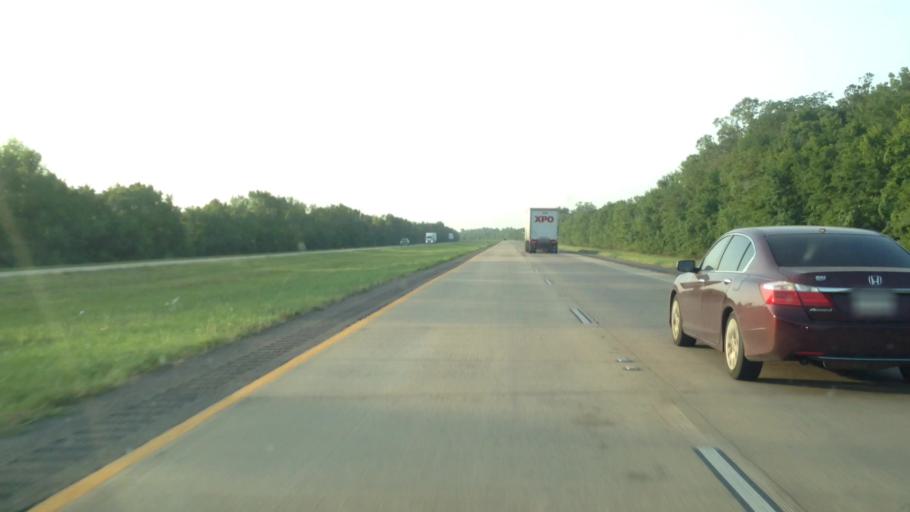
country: US
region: Louisiana
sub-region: Natchitoches Parish
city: Vienna Bend
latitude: 31.5854
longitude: -93.0284
